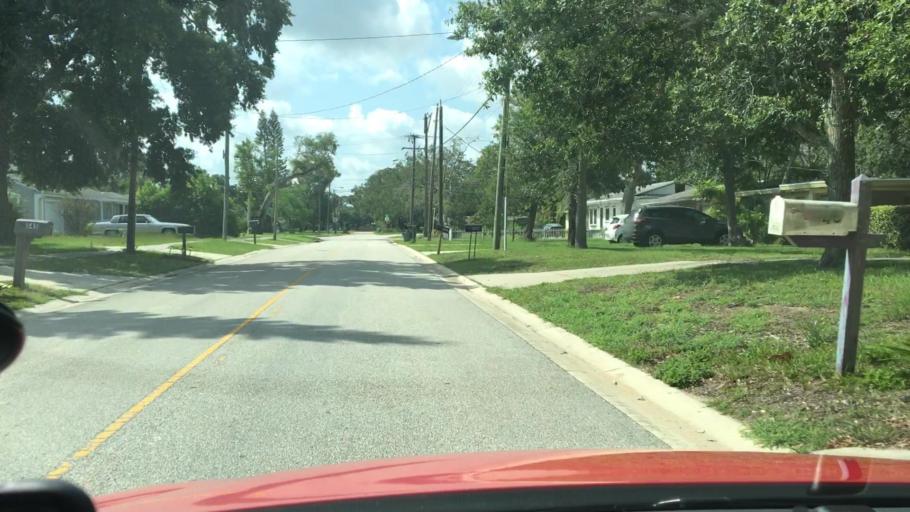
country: US
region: Florida
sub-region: Volusia County
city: Ormond Beach
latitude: 29.2706
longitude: -81.0518
